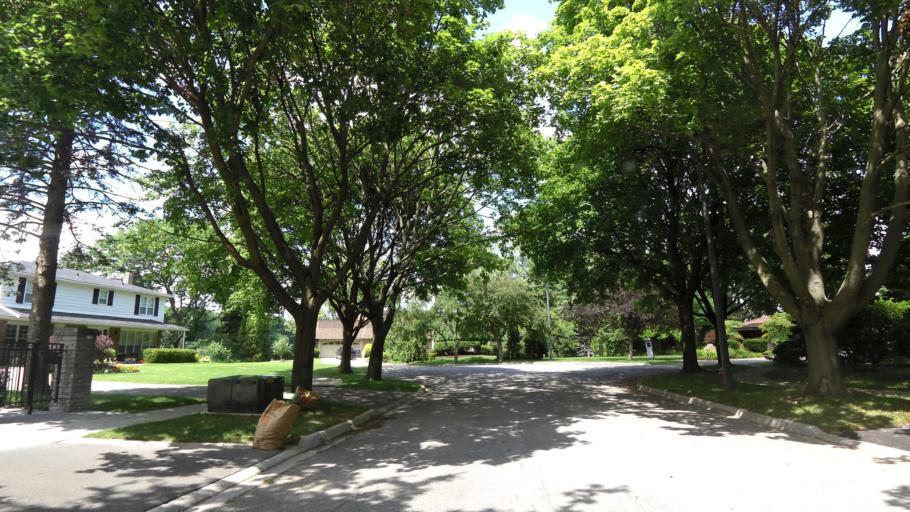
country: CA
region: Ontario
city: Mississauga
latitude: 43.5155
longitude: -79.6031
